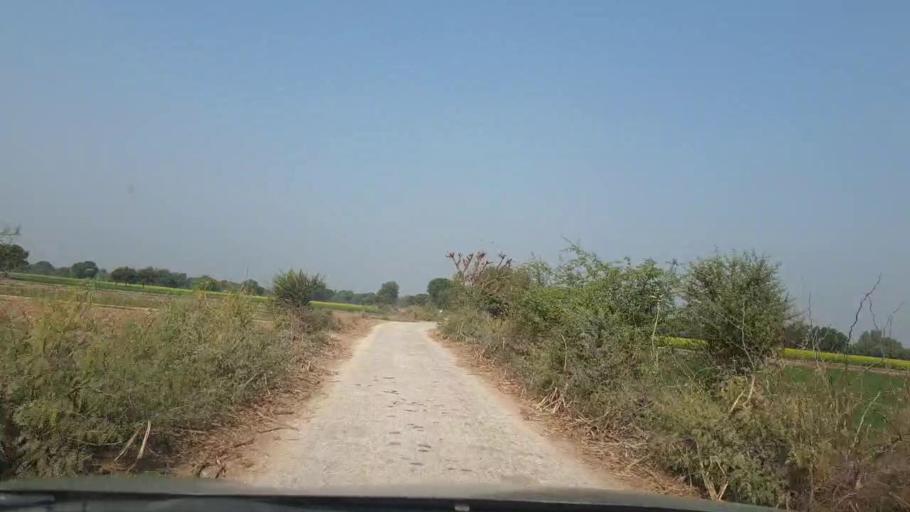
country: PK
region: Sindh
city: Tando Allahyar
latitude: 25.5282
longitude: 68.7838
